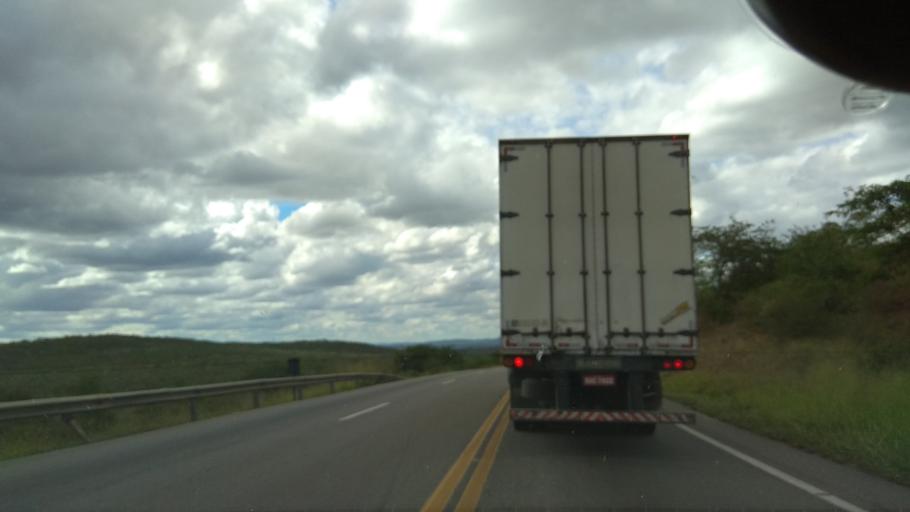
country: BR
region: Bahia
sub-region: Santa Ines
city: Santa Ines
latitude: -13.0378
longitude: -39.9678
